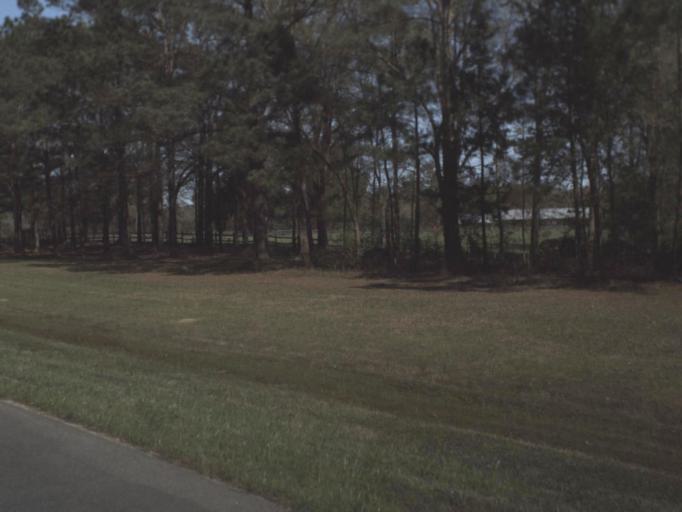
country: US
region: Florida
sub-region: Holmes County
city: Bonifay
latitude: 30.7492
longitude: -85.8939
